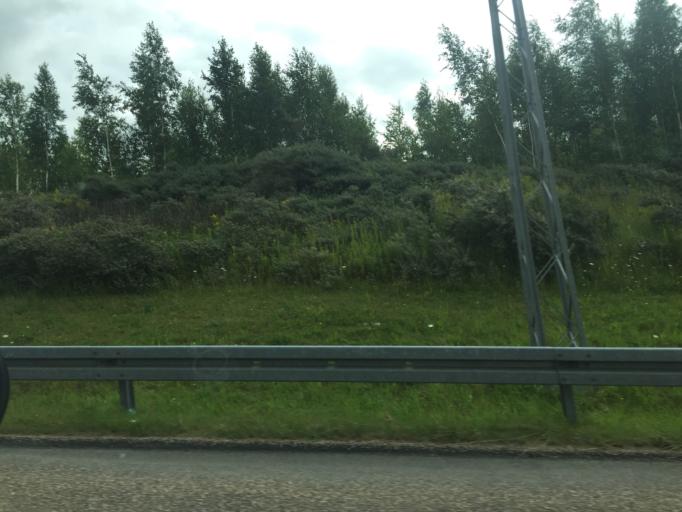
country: DK
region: Capital Region
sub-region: Kobenhavn
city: Copenhagen
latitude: 55.6321
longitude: 12.5451
